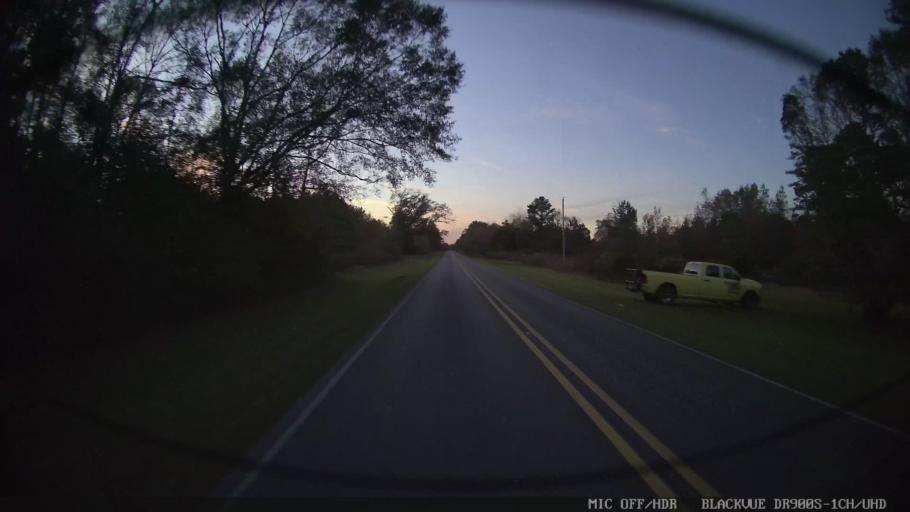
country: US
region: Mississippi
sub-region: Perry County
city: New Augusta
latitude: 31.0711
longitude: -89.1998
